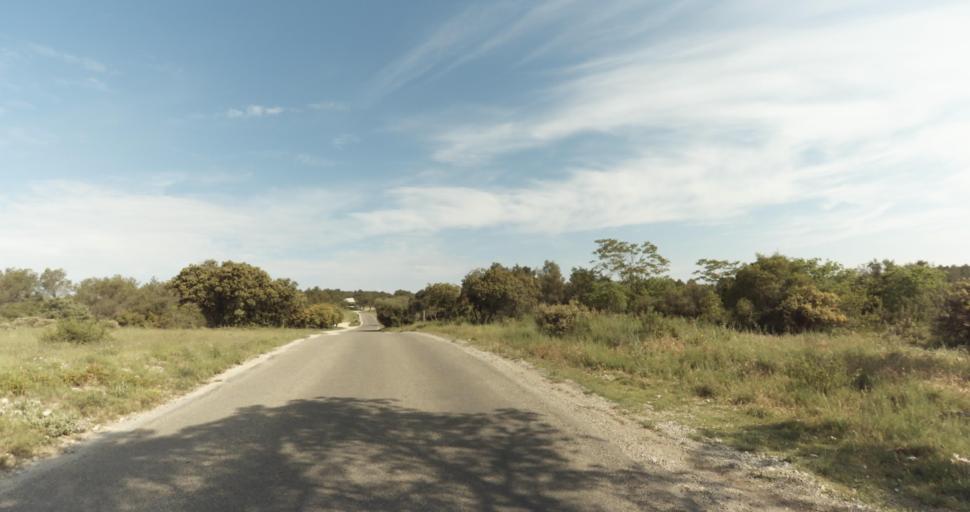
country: FR
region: Languedoc-Roussillon
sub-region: Departement du Gard
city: Poulx
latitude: 43.8756
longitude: 4.3923
